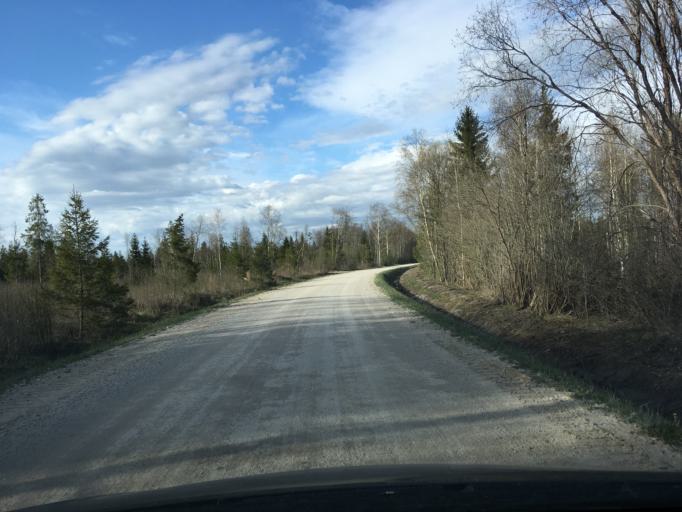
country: EE
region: Raplamaa
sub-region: Maerjamaa vald
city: Marjamaa
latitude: 58.9941
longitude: 24.3676
